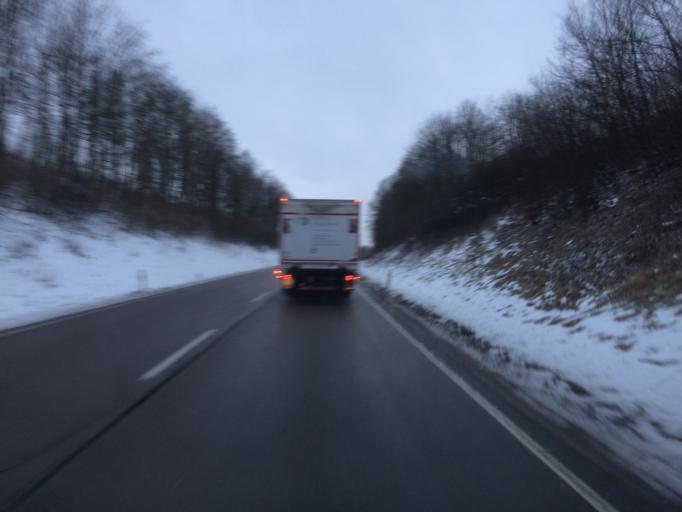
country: DE
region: Bavaria
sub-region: Upper Palatinate
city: Schwandorf in Bayern
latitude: 49.3473
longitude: 12.0824
